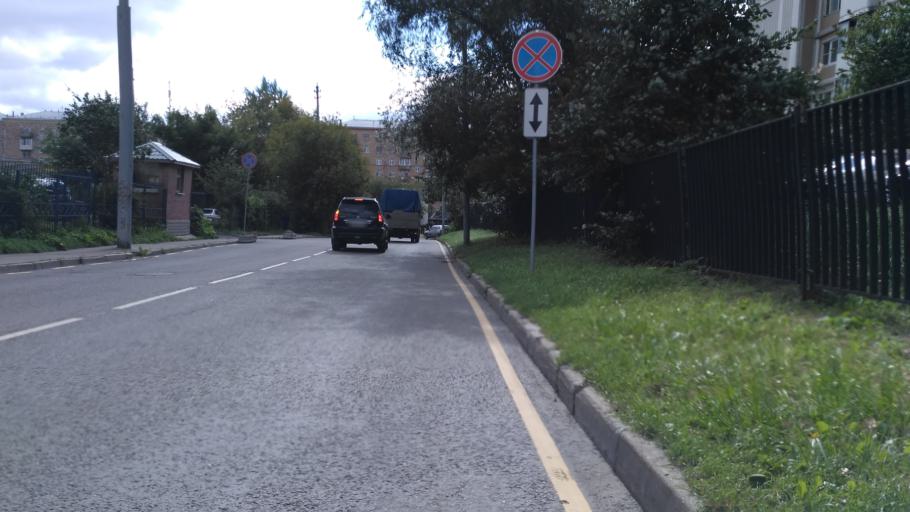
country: RU
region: Moscow
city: Ostankinskiy
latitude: 55.8231
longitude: 37.6299
